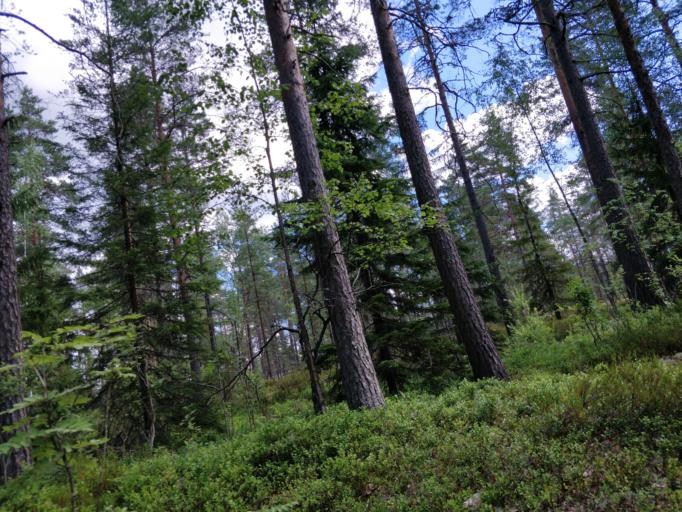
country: FI
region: Uusimaa
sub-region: Helsinki
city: Vihti
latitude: 60.3129
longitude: 24.4707
